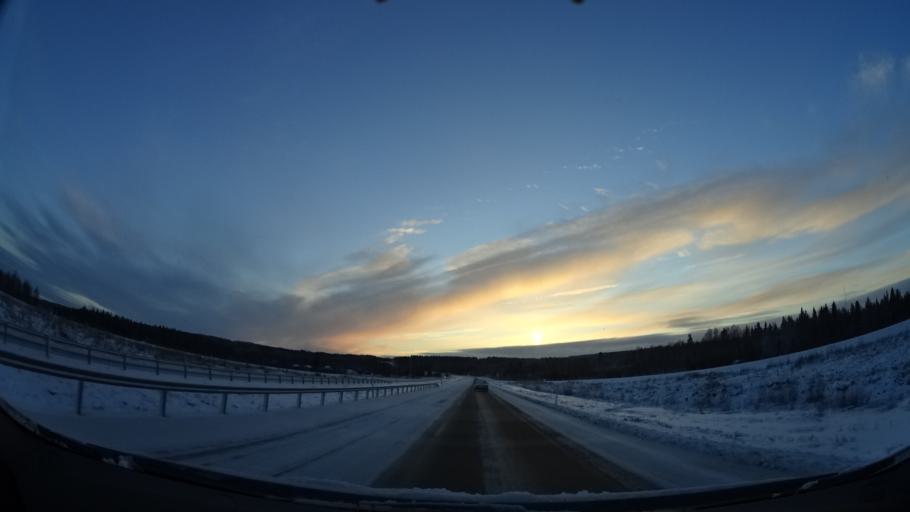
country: SE
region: Vaesterbotten
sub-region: Skelleftea Kommun
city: Kage
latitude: 64.7887
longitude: 21.0203
